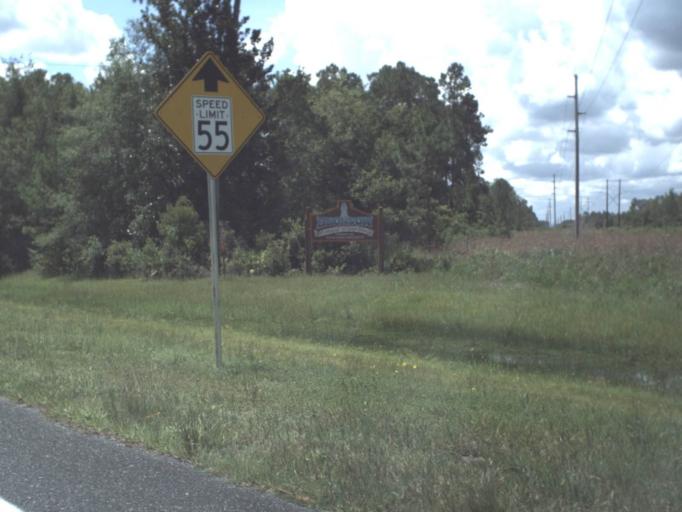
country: US
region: Florida
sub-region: Levy County
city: Bronson
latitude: 29.4561
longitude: -82.6547
